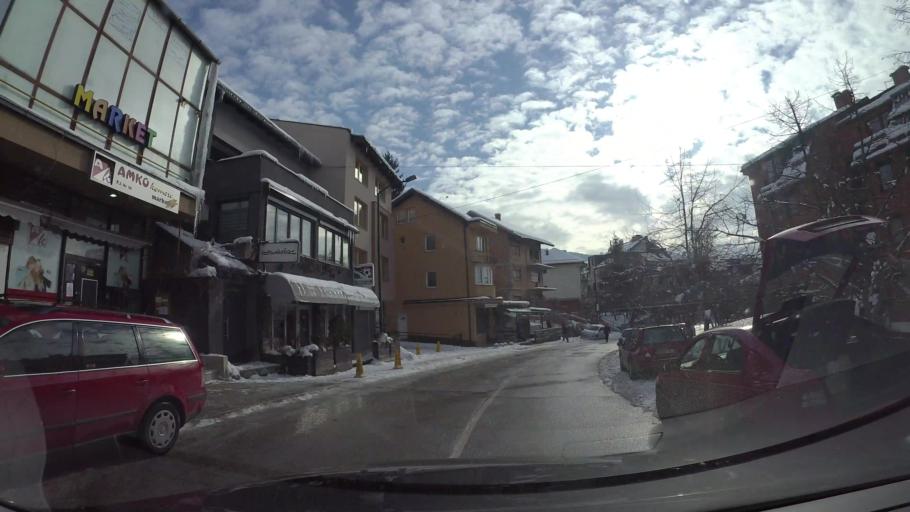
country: BA
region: Federation of Bosnia and Herzegovina
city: Kobilja Glava
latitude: 43.8715
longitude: 18.4213
